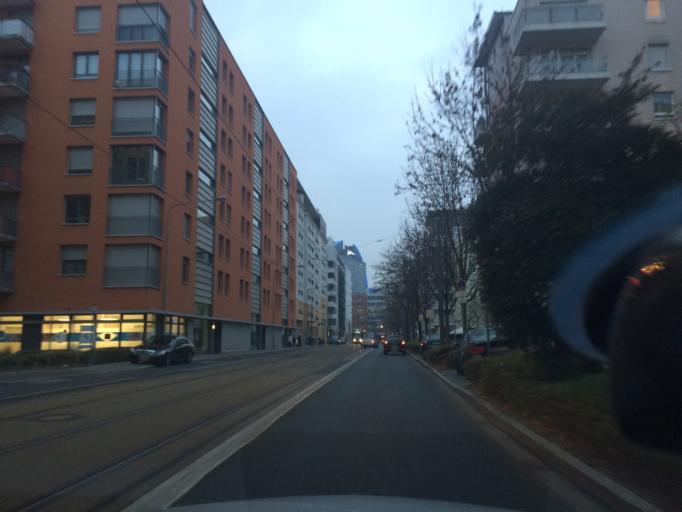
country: DE
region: Hesse
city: Niederrad
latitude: 50.1170
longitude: 8.6342
